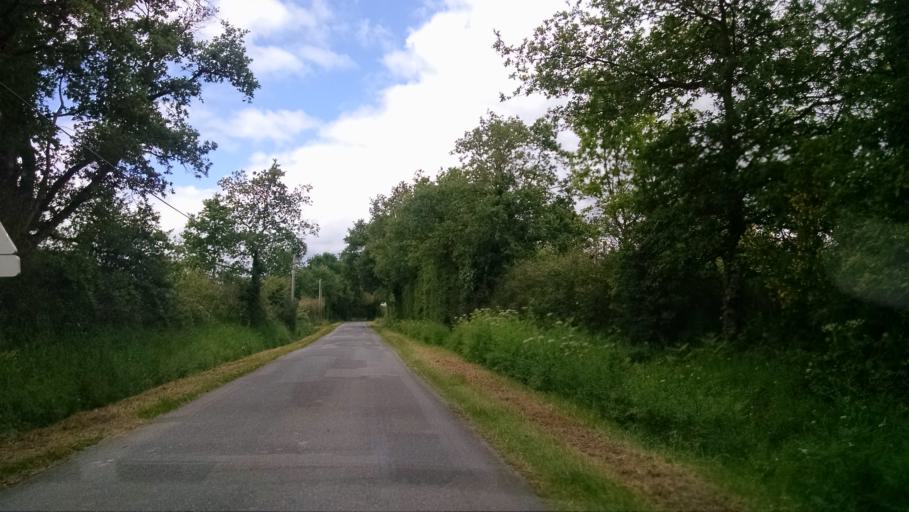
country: FR
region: Pays de la Loire
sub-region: Departement de la Loire-Atlantique
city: Remouille
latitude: 47.0335
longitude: -1.3843
